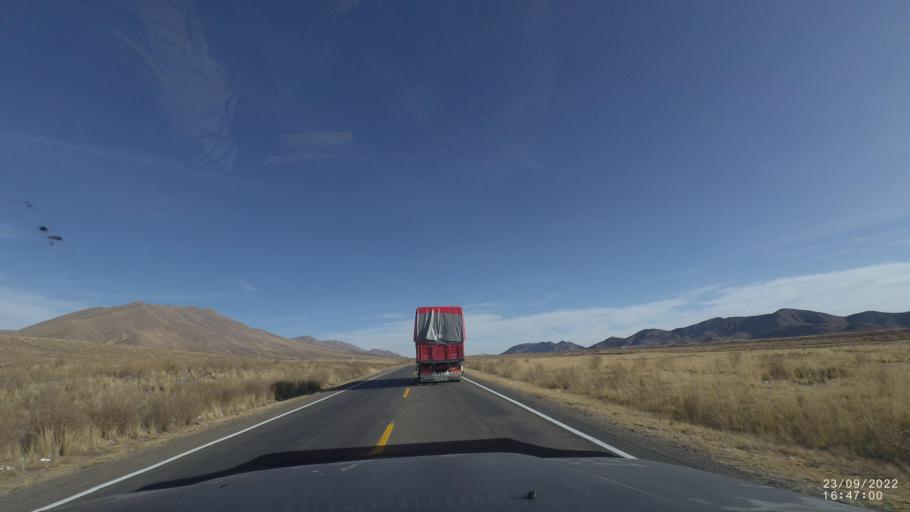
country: BO
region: Oruro
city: Poopo
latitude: -18.3637
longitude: -66.9826
